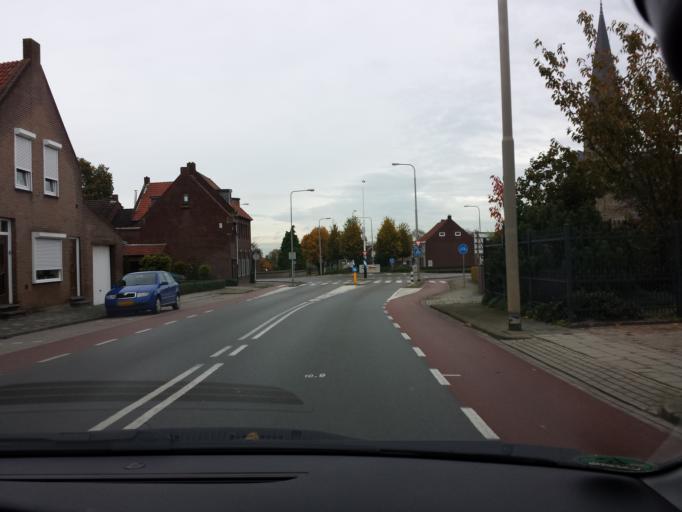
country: NL
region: Limburg
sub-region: Gemeente Echt-Susteren
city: Koningsbosch
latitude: 51.0508
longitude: 5.9577
